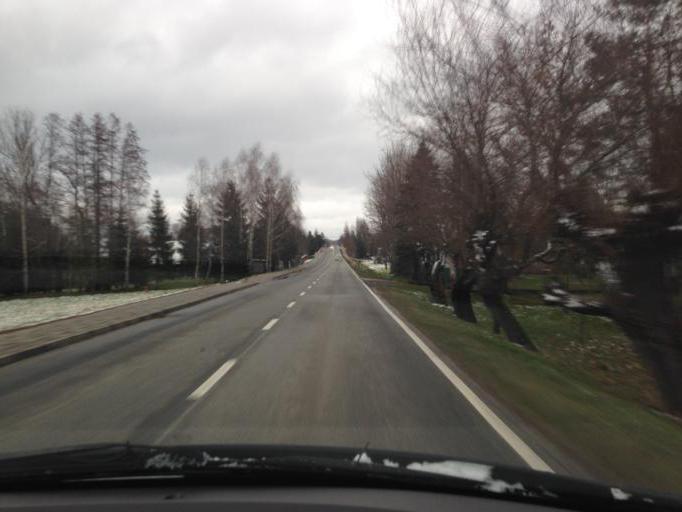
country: PL
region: Lesser Poland Voivodeship
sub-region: Powiat tarnowski
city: Zakliczyn
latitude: 49.8545
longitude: 20.8209
